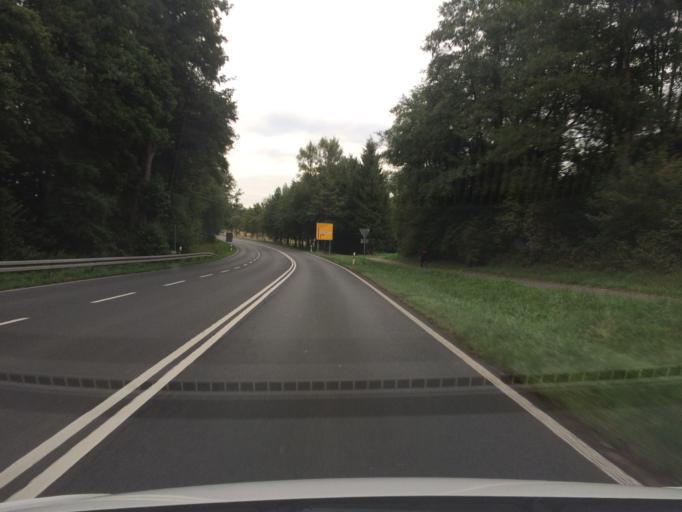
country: DE
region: Bavaria
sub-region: Regierungsbezirk Unterfranken
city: Hosbach
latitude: 50.0067
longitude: 9.2266
